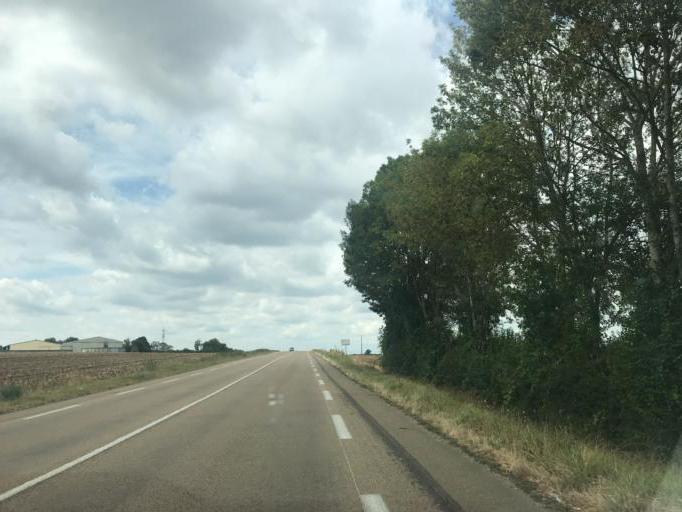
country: FR
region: Bourgogne
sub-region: Departement de l'Yonne
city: Avallon
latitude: 47.4967
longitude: 3.9494
